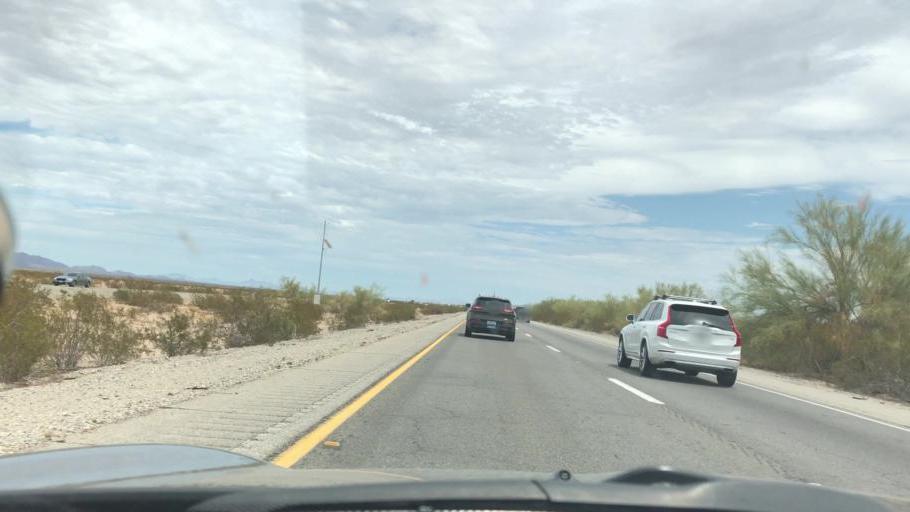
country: US
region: California
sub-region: Riverside County
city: Mesa Verde
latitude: 33.6147
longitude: -115.0154
